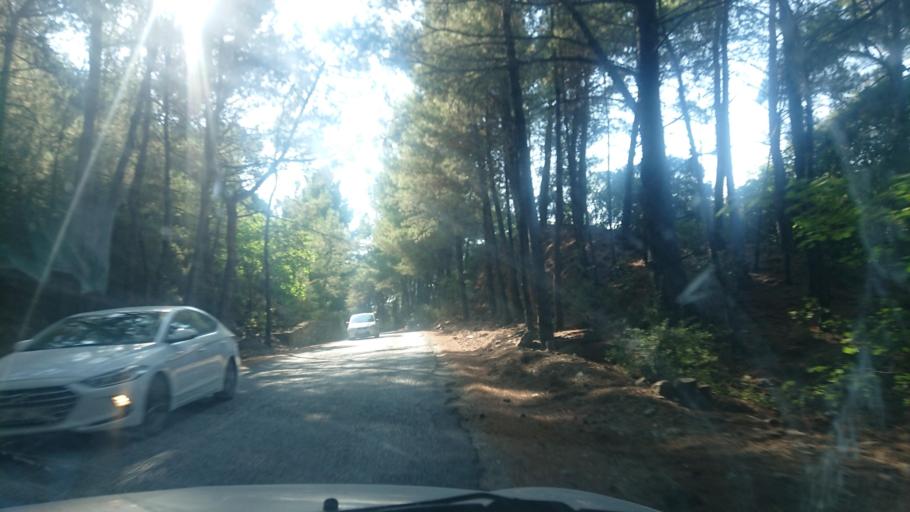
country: TR
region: Aydin
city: Atburgazi
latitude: 37.6884
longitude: 27.1273
